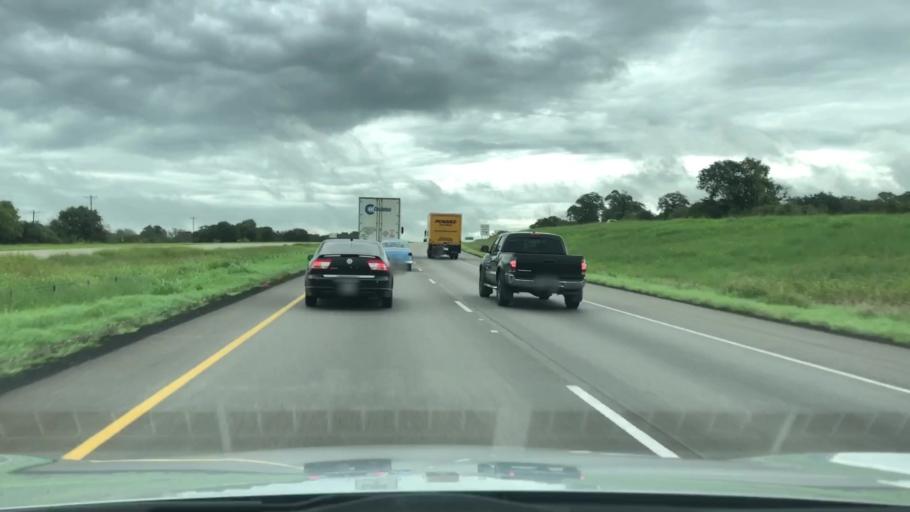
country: US
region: Texas
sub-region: Caldwell County
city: Luling
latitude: 29.6541
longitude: -97.5804
